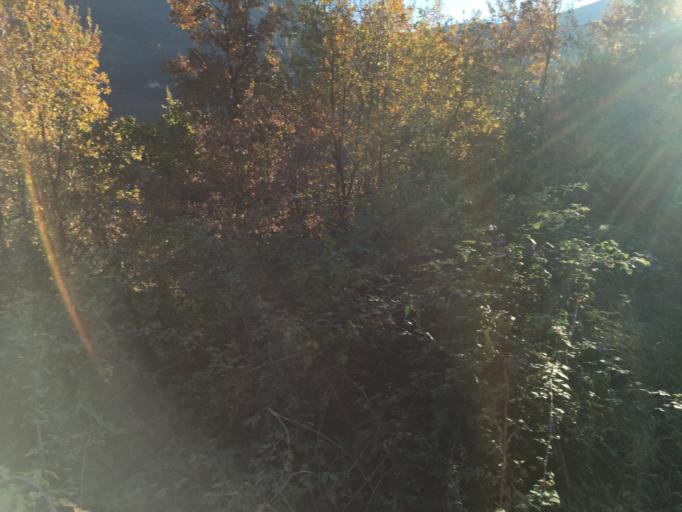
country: IT
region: Campania
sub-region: Provincia di Salerno
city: Salvitelle
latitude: 40.6011
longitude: 15.4809
